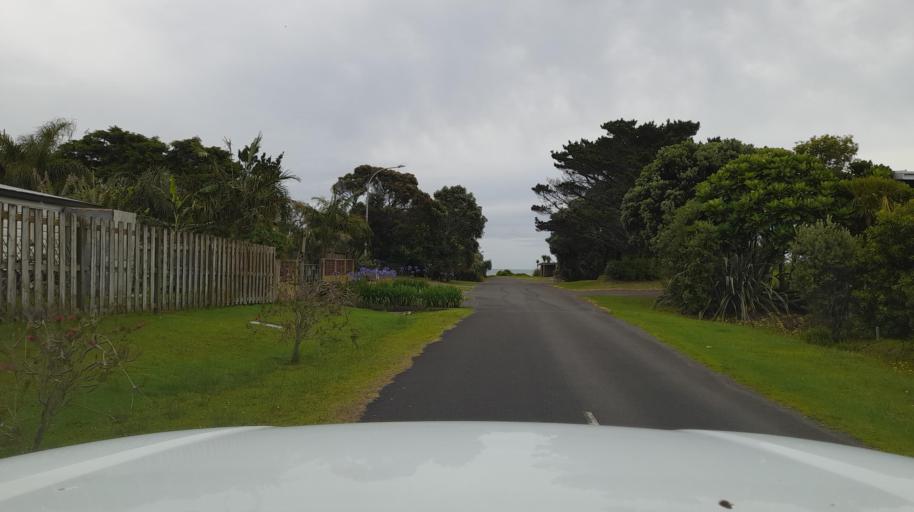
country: NZ
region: Northland
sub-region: Far North District
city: Ahipara
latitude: -35.1676
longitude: 173.1538
